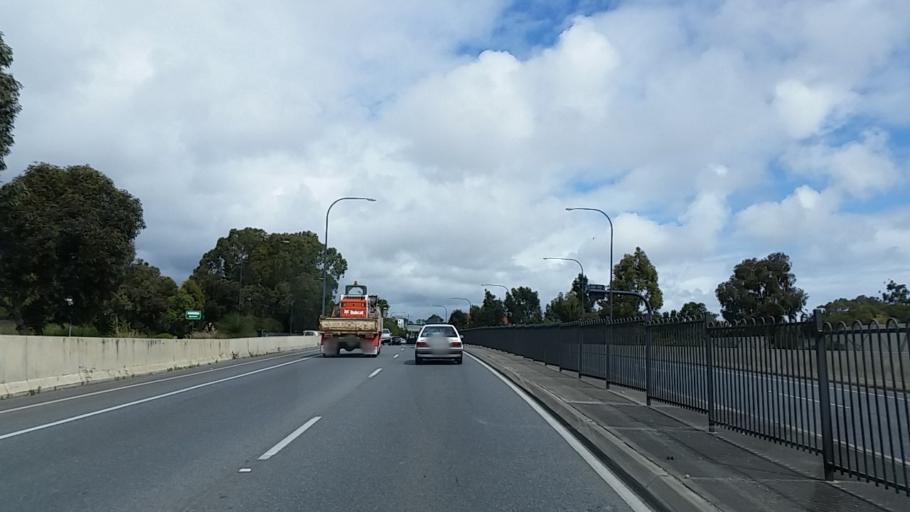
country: AU
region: South Australia
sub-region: Unley
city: Forestville
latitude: -34.9548
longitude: 138.5716
